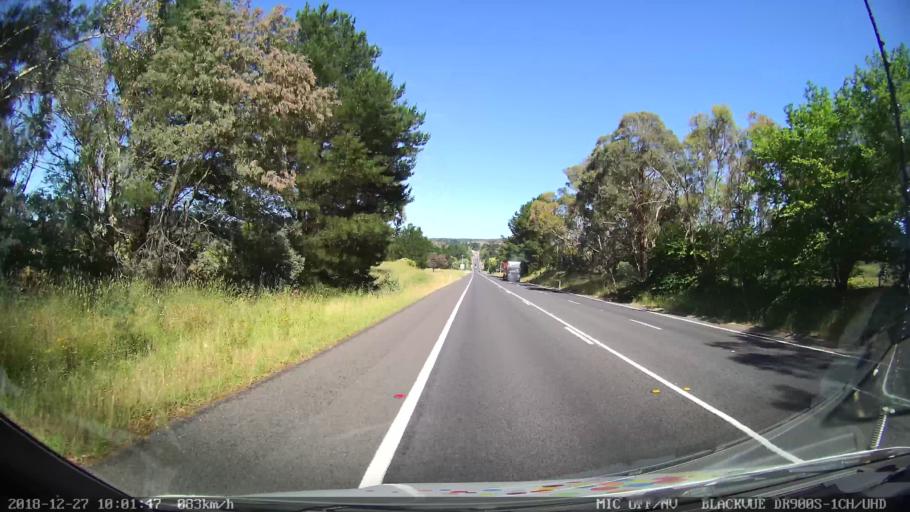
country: AU
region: New South Wales
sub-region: Lithgow
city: Portland
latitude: -33.4384
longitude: 149.9325
